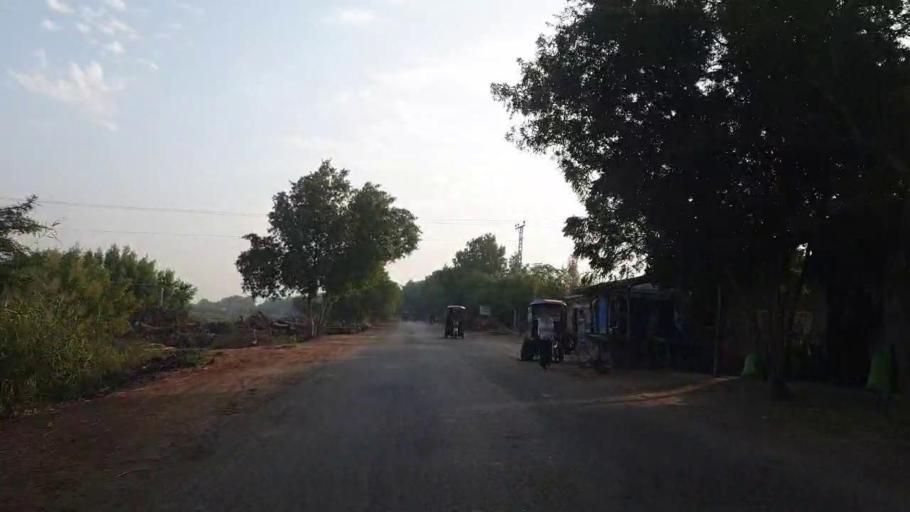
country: PK
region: Sindh
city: Badin
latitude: 24.6790
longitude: 68.9068
